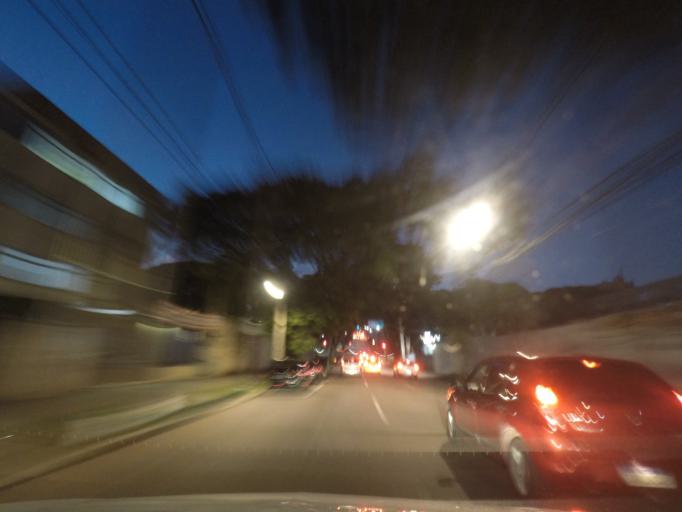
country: BR
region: Parana
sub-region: Curitiba
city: Curitiba
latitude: -25.4486
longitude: -49.2786
